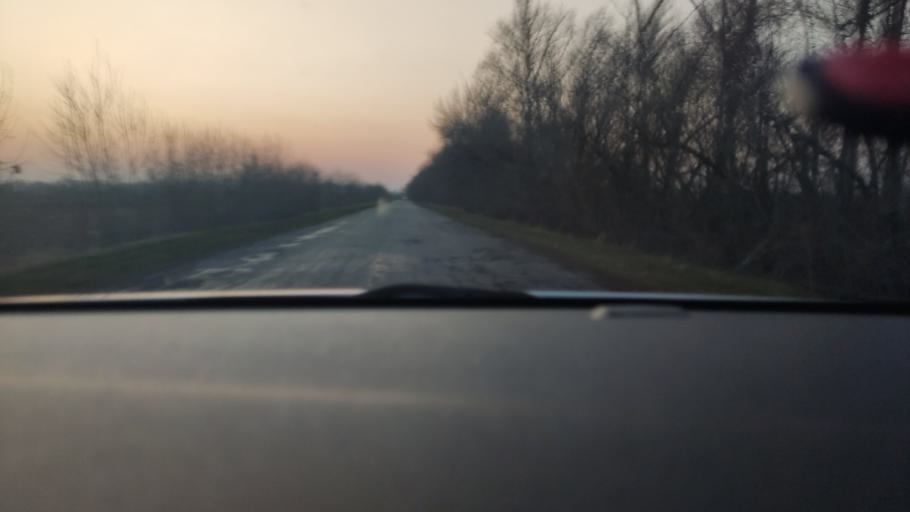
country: RU
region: Voronezj
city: Uryv-Pokrovka
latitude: 51.1460
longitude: 39.0629
